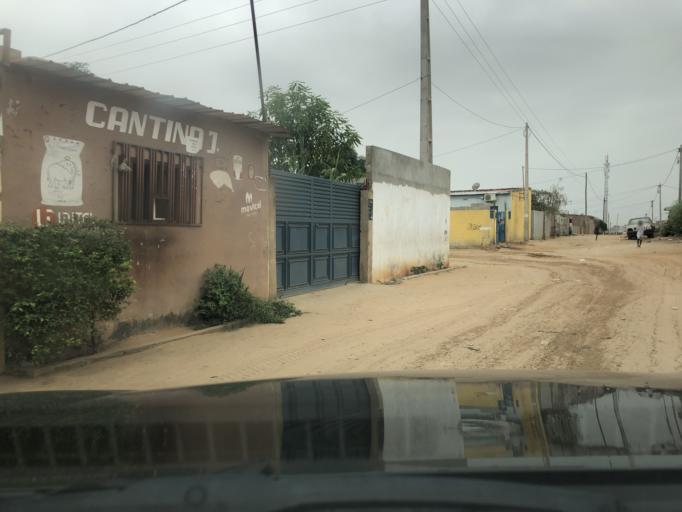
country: AO
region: Luanda
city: Luanda
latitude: -8.9375
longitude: 13.2334
